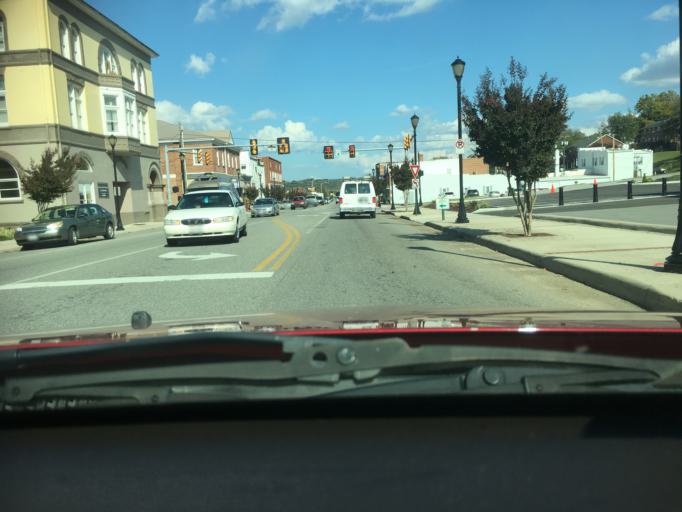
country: US
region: Virginia
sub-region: City of Radford
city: Radford
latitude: 37.1339
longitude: -80.5756
